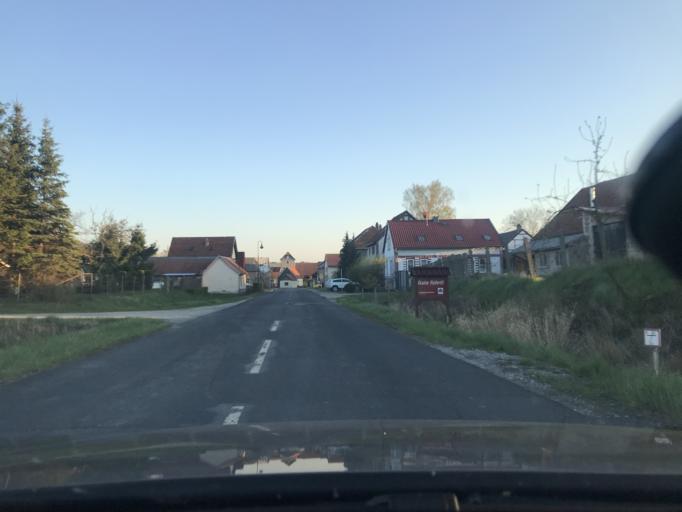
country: DE
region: Thuringia
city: Sollstedt
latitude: 51.2745
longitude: 10.5126
